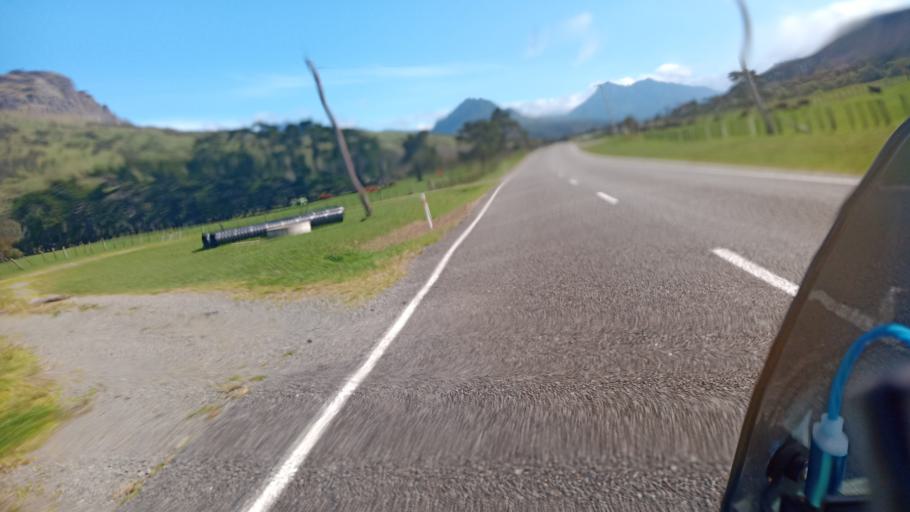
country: NZ
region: Gisborne
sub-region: Gisborne District
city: Gisborne
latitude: -37.8658
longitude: 178.2122
